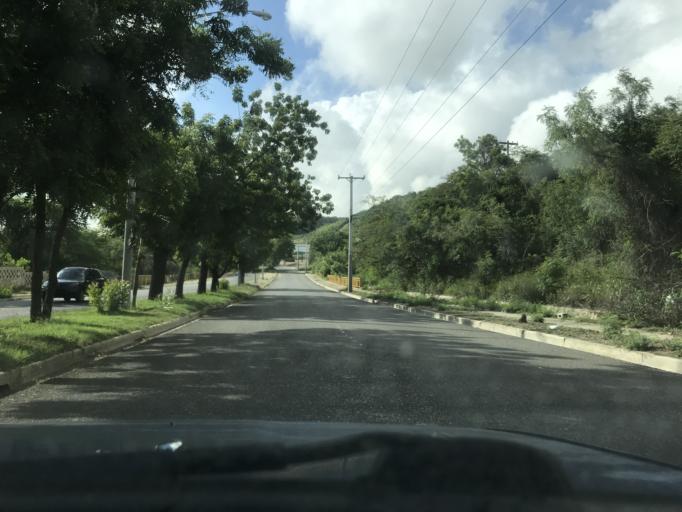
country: DO
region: Santiago
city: Santiago de los Caballeros
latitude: 19.4153
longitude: -70.7303
